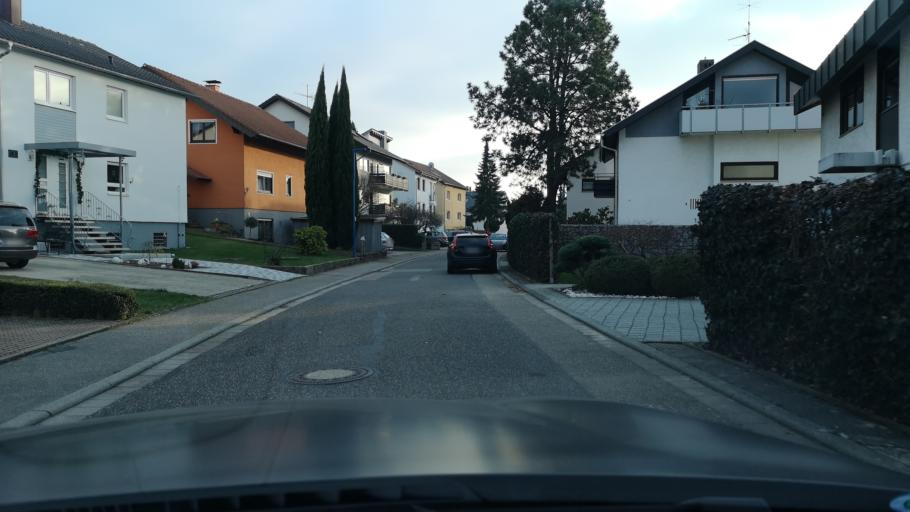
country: DE
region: Baden-Wuerttemberg
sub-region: Karlsruhe Region
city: Ettlingen
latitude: 48.9345
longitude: 8.4653
